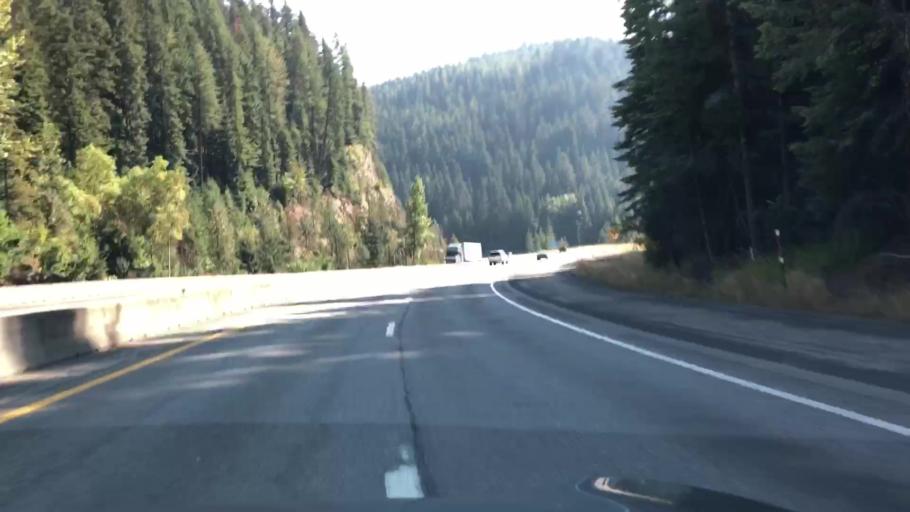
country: US
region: Idaho
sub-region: Shoshone County
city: Pinehurst
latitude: 47.5958
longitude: -116.4923
